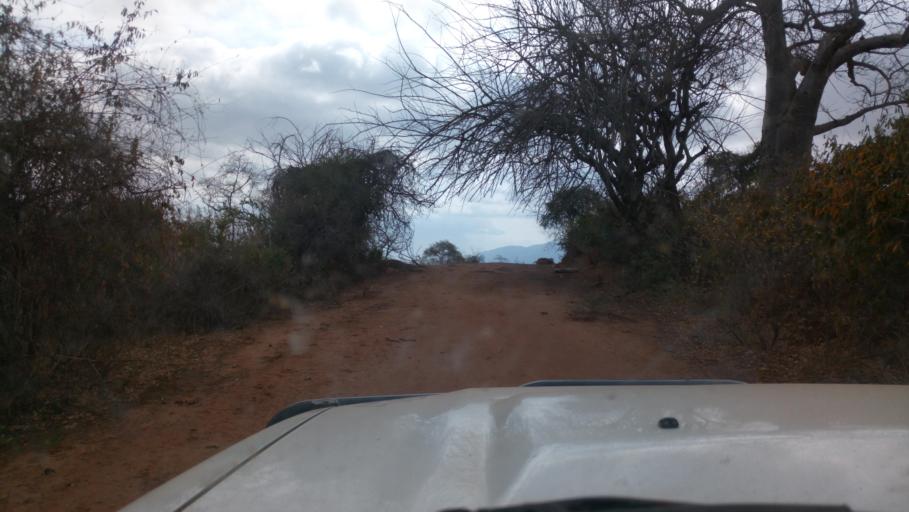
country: KE
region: Kitui
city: Kitui
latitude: -1.8436
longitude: 38.2955
